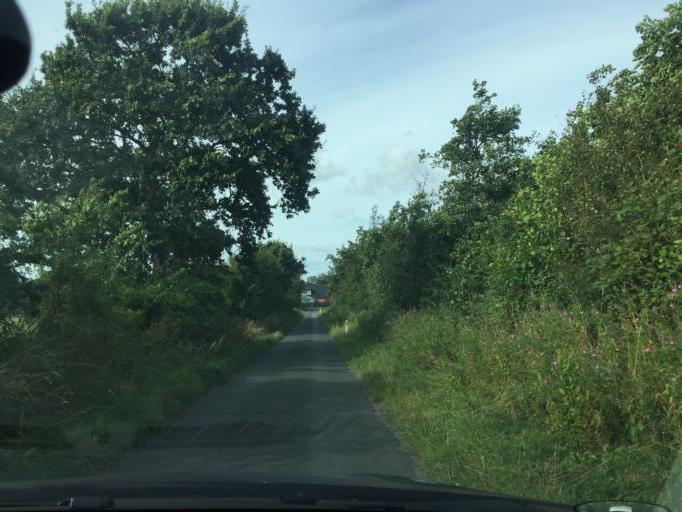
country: DK
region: South Denmark
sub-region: Faaborg-Midtfyn Kommune
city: Arslev
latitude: 55.3481
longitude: 10.5133
